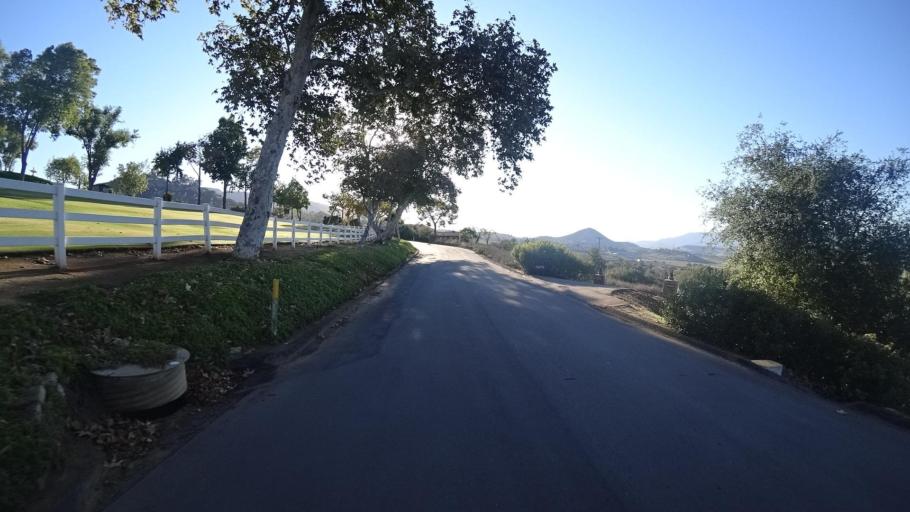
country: US
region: California
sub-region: San Diego County
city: Jamul
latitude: 32.7134
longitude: -116.8633
